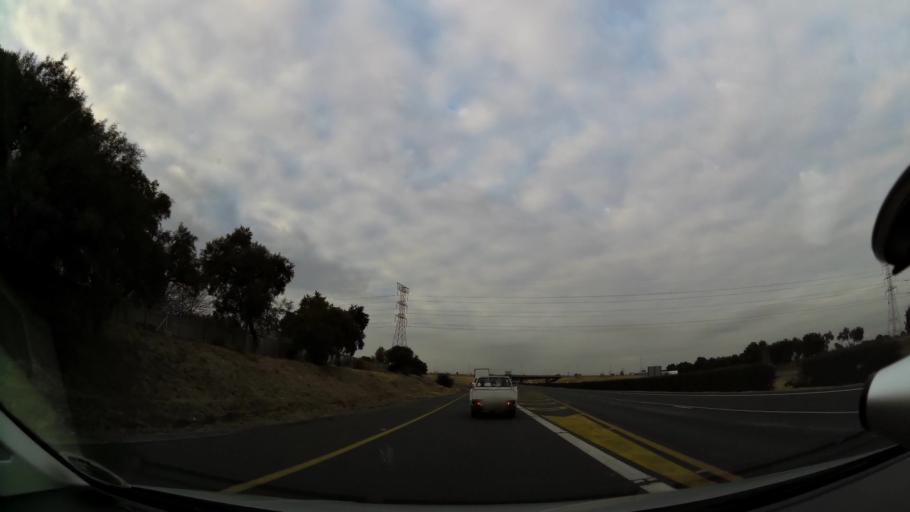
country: ZA
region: Orange Free State
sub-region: Mangaung Metropolitan Municipality
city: Bloemfontein
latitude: -29.1235
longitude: 26.1630
